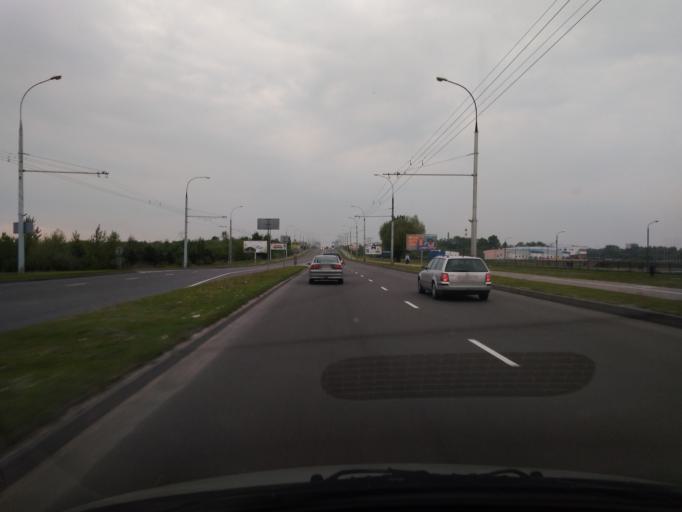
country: BY
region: Brest
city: Brest
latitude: 52.0812
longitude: 23.7378
